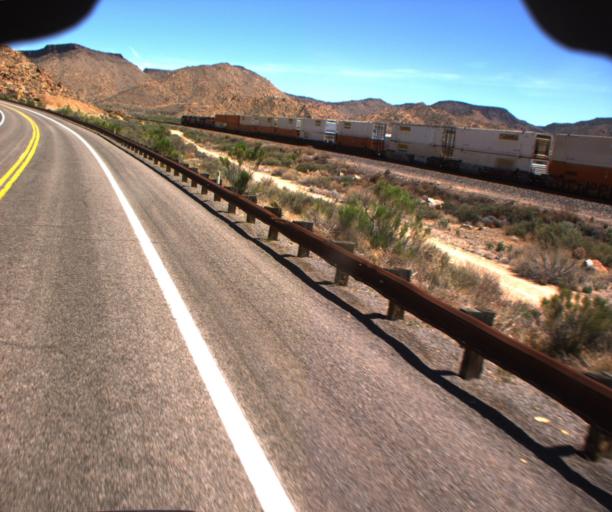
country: US
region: Arizona
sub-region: Mohave County
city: Peach Springs
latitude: 35.3675
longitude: -113.6734
